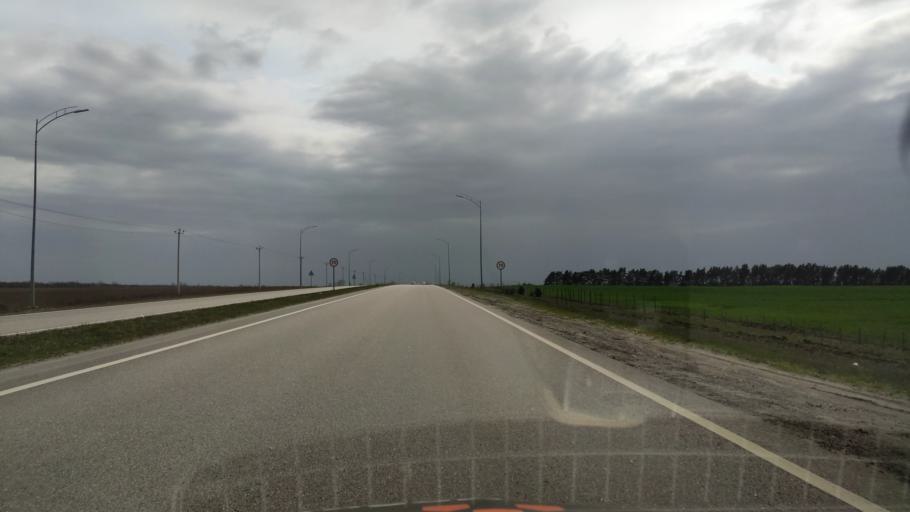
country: RU
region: Belgorod
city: Staryy Oskol
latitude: 51.3992
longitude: 37.8744
